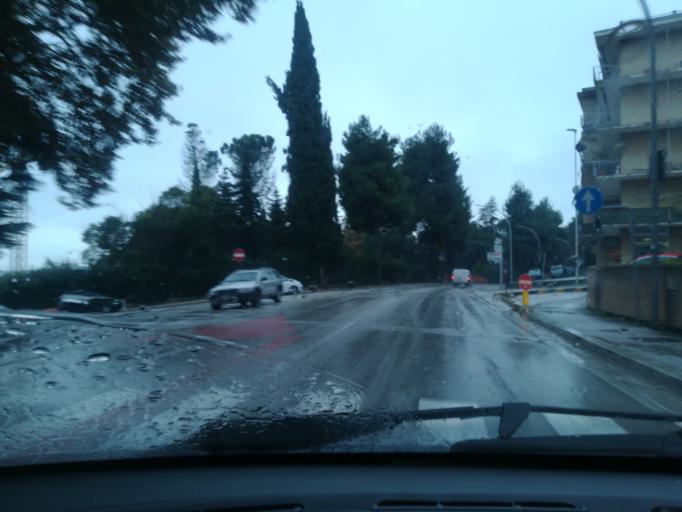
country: IT
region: The Marches
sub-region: Provincia di Macerata
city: Macerata
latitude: 43.2929
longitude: 13.4372
